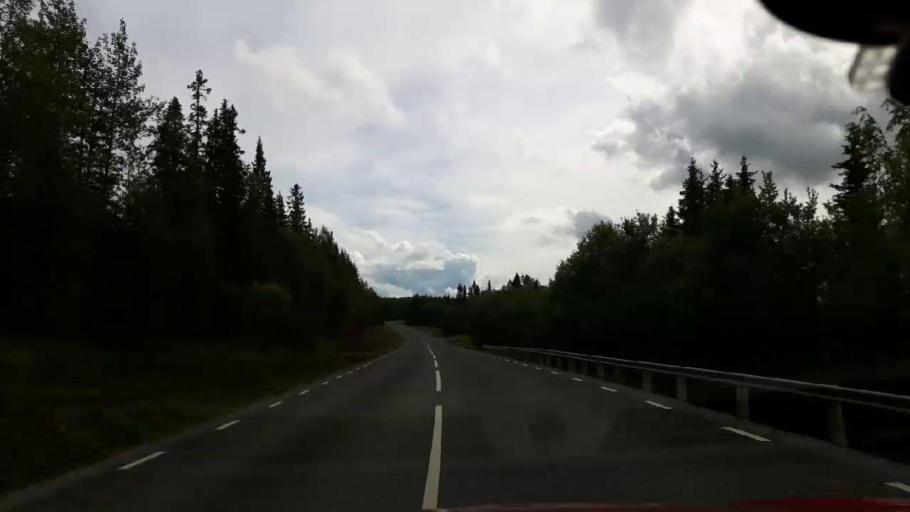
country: NO
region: Nord-Trondelag
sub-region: Lierne
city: Sandvika
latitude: 64.5907
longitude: 14.1160
